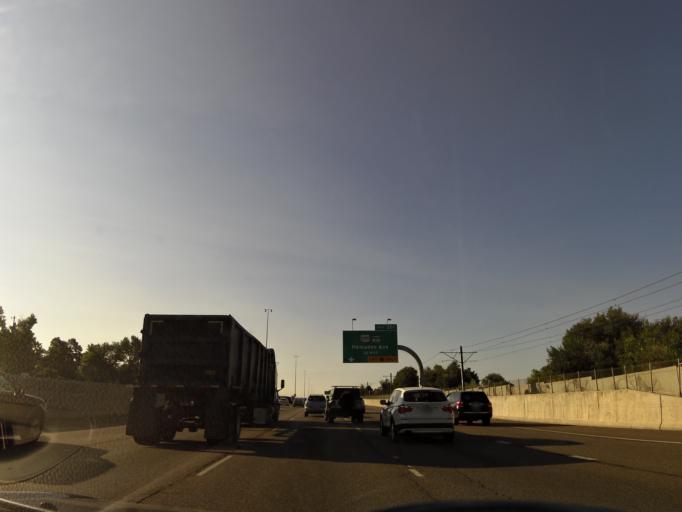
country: US
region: Colorado
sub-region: Arapahoe County
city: Cherry Hills Village
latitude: 39.6621
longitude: -104.9224
